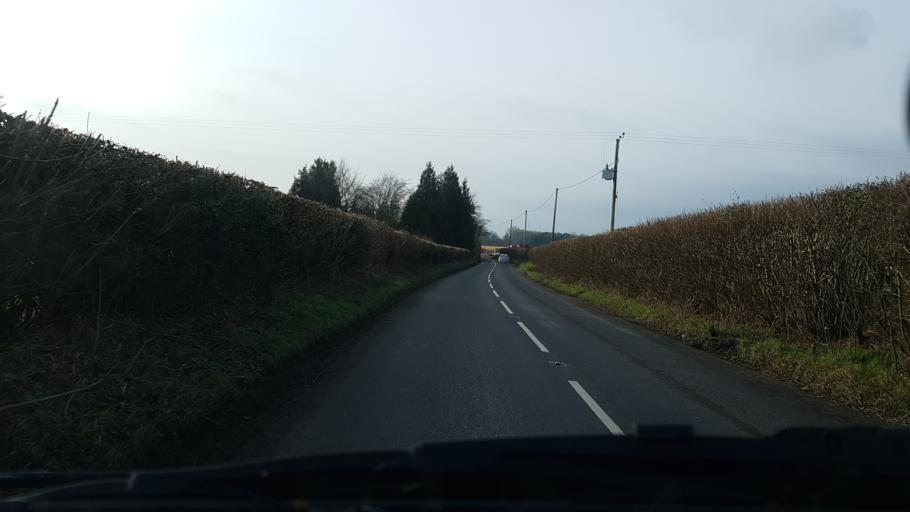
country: GB
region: England
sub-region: Wiltshire
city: Pewsey
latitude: 51.3473
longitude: -1.7332
